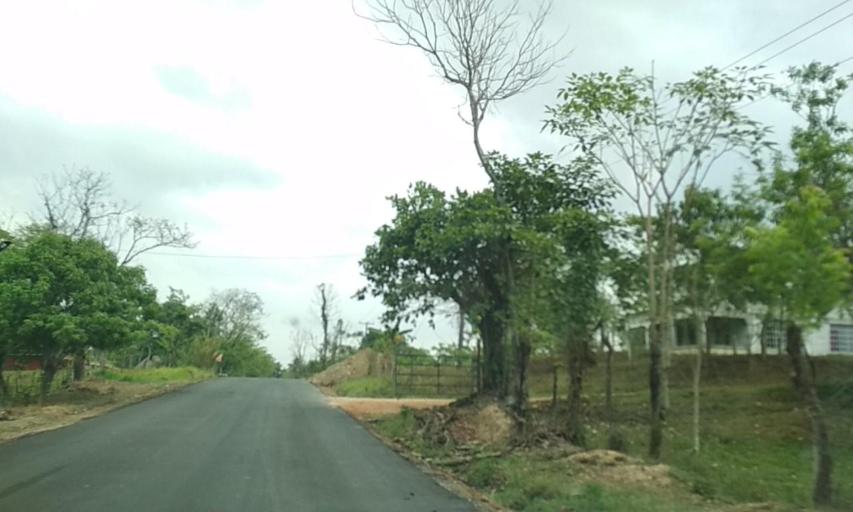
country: MX
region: Tabasco
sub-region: Huimanguillo
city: Francisco Rueda
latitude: 17.6864
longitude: -94.0919
